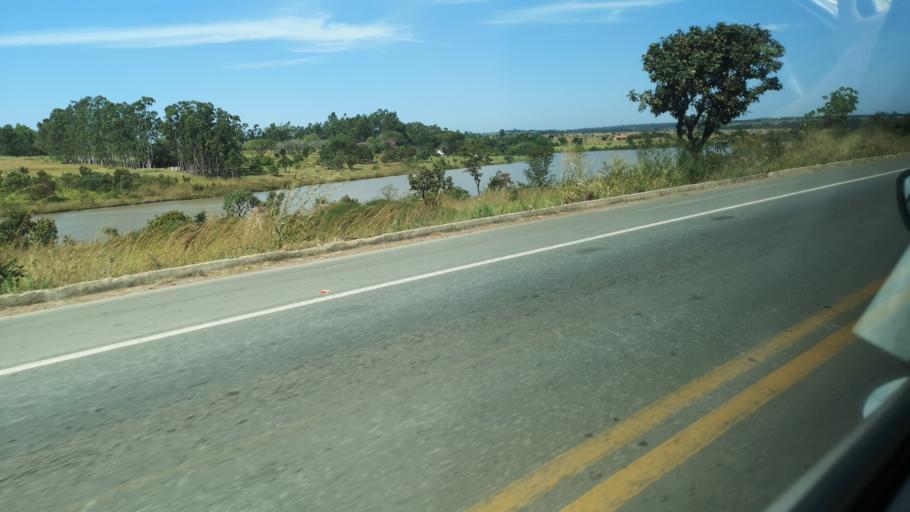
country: BR
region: Goias
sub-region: Senador Canedo
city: Senador Canedo
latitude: -16.7302
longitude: -49.1133
